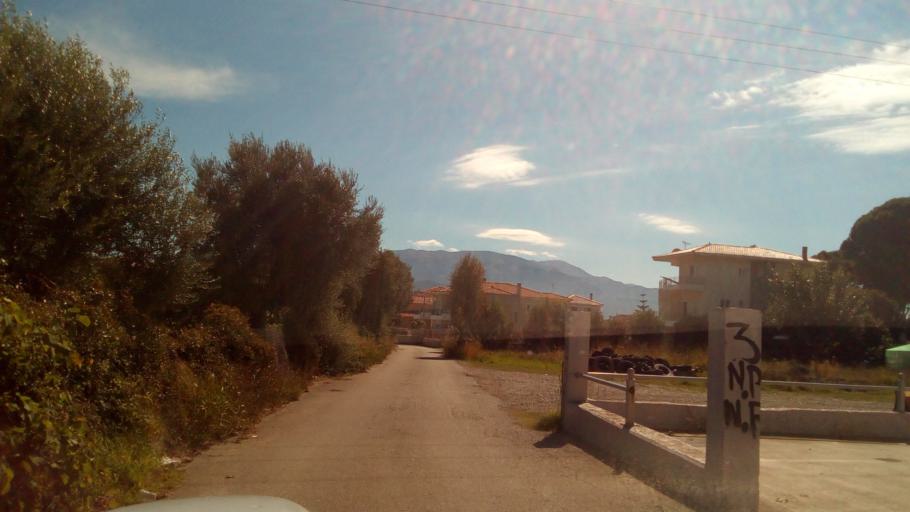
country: GR
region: West Greece
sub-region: Nomos Aitolias kai Akarnanias
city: Nafpaktos
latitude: 38.3807
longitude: 21.8005
